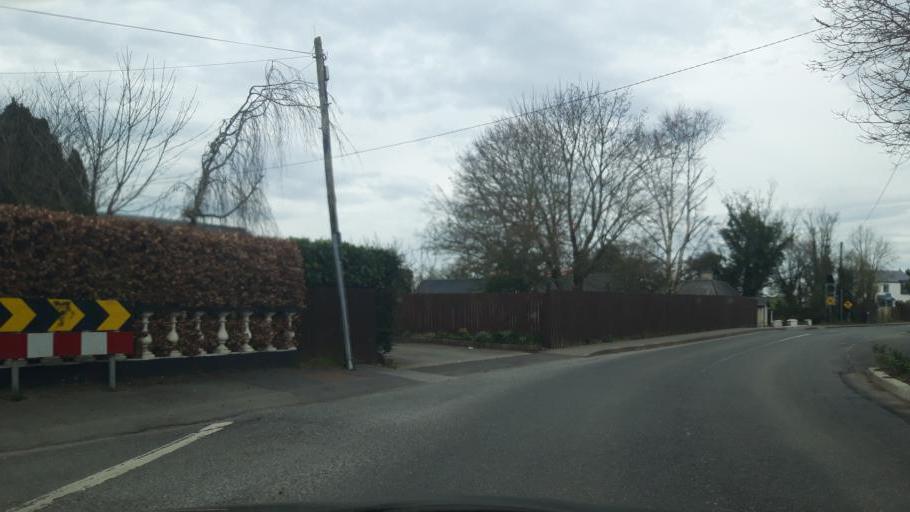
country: IE
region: Leinster
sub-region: Kildare
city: Clane
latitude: 53.3341
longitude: -6.6792
